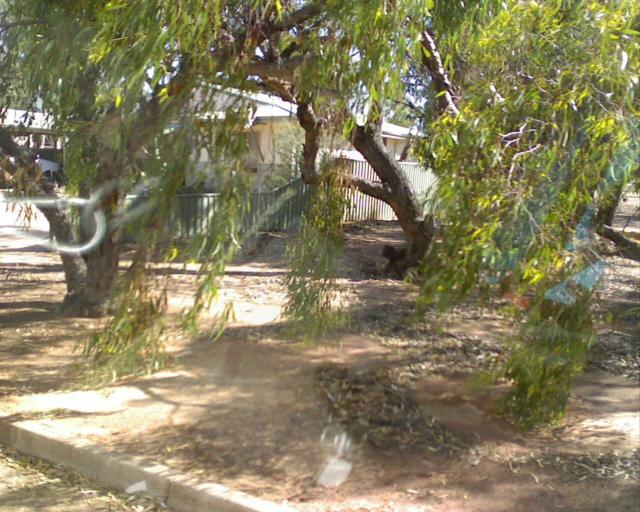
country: AU
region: Western Australia
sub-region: Moora
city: Moora
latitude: -29.9863
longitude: 116.5688
